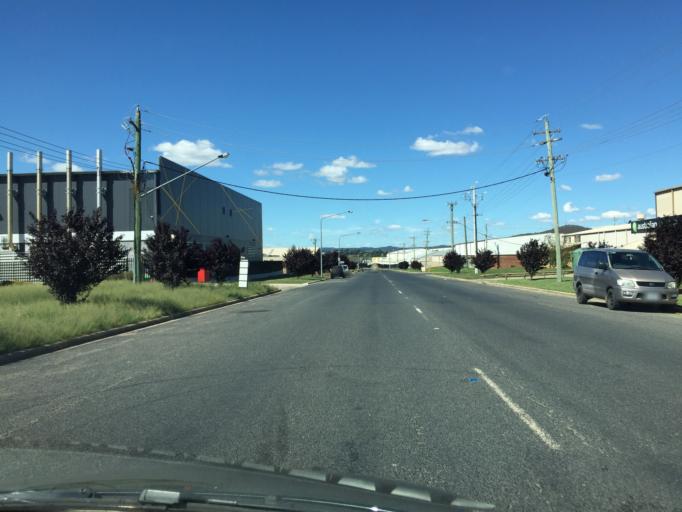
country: AU
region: Australian Capital Territory
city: Macarthur
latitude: -35.3903
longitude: 149.1681
